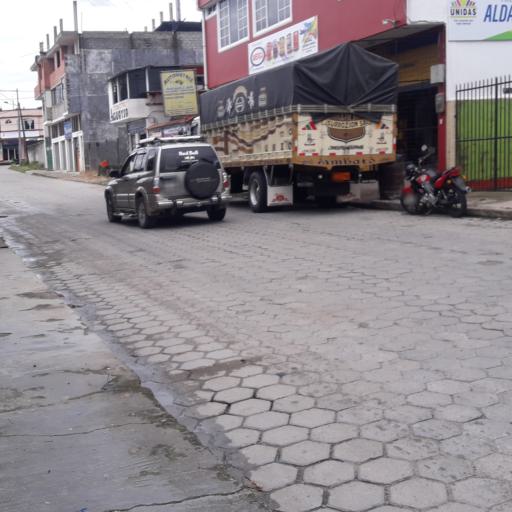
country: EC
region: Napo
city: Tena
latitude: -1.0012
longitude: -77.8108
